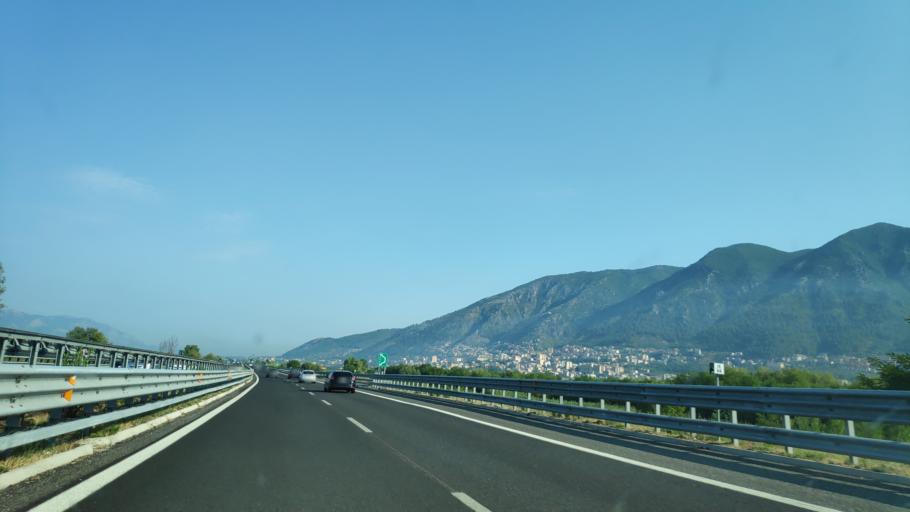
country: IT
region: Campania
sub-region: Provincia di Salerno
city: Sala Consilina
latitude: 40.3747
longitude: 15.5990
